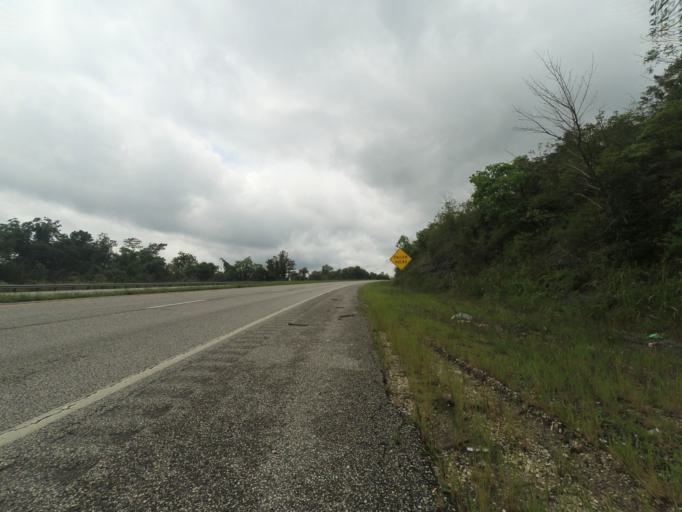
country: US
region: West Virginia
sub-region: Cabell County
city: Huntington
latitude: 38.4298
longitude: -82.4610
